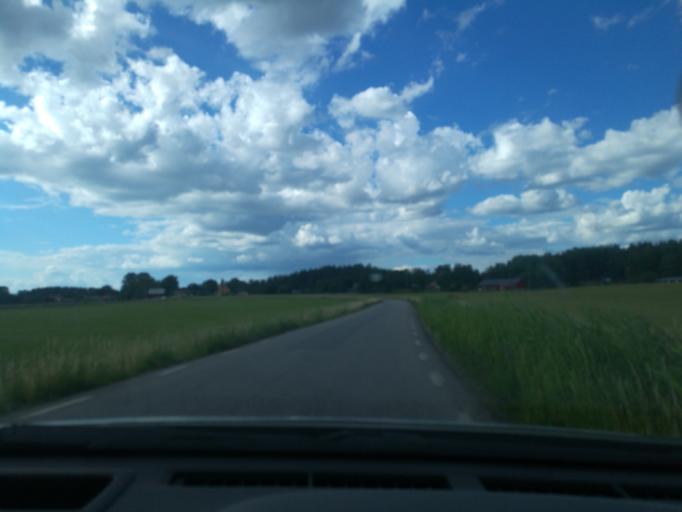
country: SE
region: Soedermanland
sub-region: Eskilstuna Kommun
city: Arla
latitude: 59.4510
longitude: 16.7369
